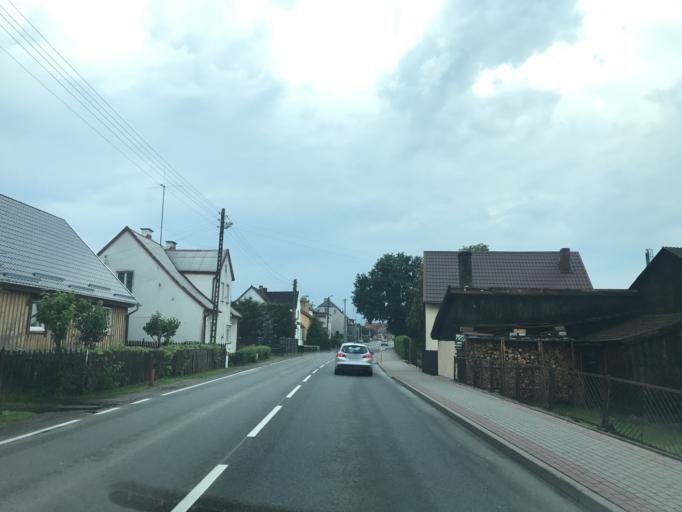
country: PL
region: Pomeranian Voivodeship
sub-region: Powiat czluchowski
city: Rzeczenica
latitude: 53.7567
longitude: 17.1117
